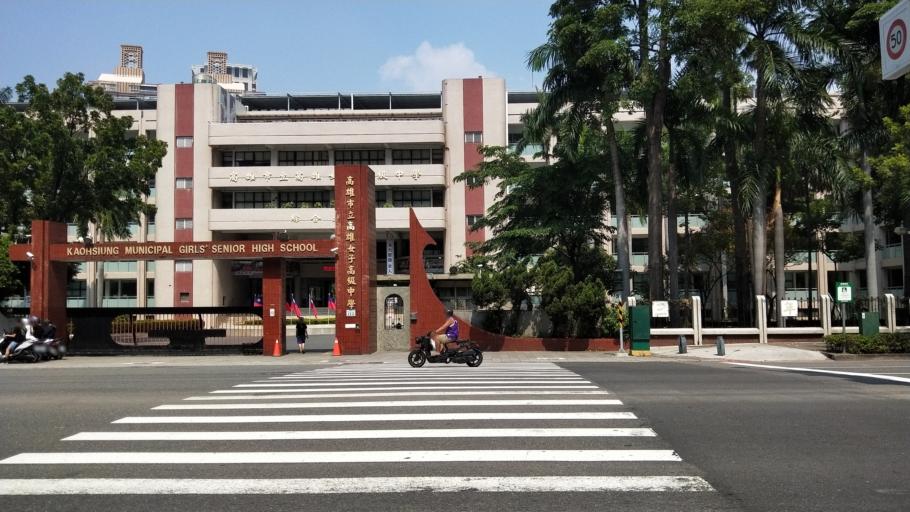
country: TW
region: Kaohsiung
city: Kaohsiung
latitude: 22.6204
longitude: 120.2930
